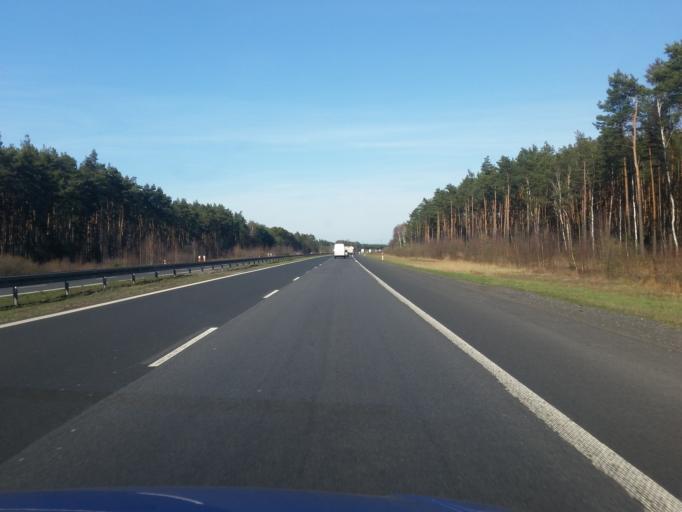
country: PL
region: Silesian Voivodeship
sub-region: Powiat czestochowski
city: Borowno
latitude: 51.0059
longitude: 19.2989
